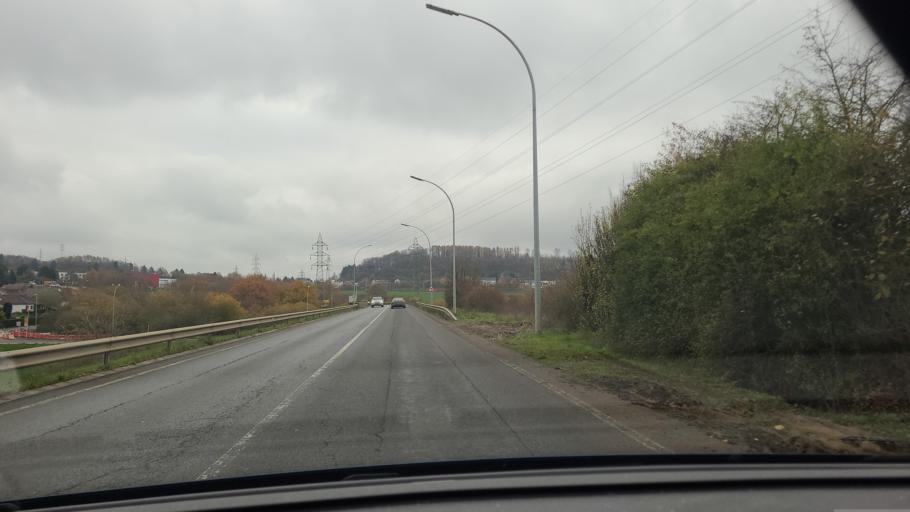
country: LU
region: Luxembourg
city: Belvaux
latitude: 49.5242
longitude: 5.9219
